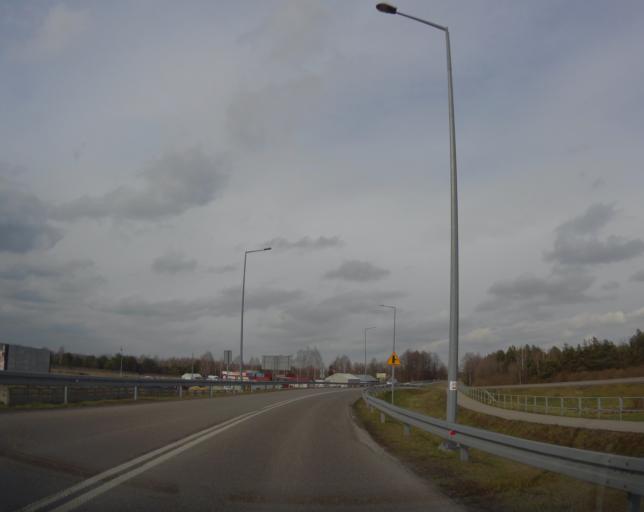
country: PL
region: Lublin Voivodeship
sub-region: Powiat bialski
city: Terespol
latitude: 52.0598
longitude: 23.6149
